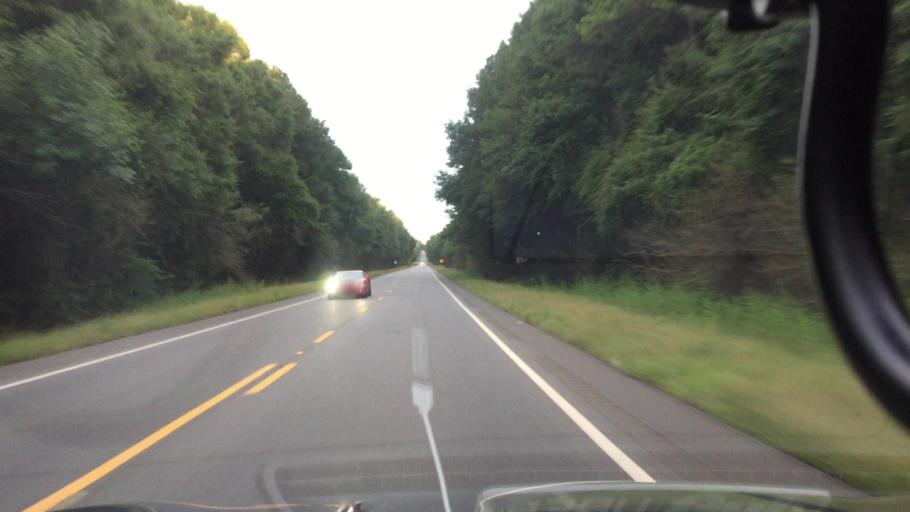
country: US
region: Alabama
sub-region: Pike County
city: Brundidge
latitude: 31.5932
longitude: -85.9442
